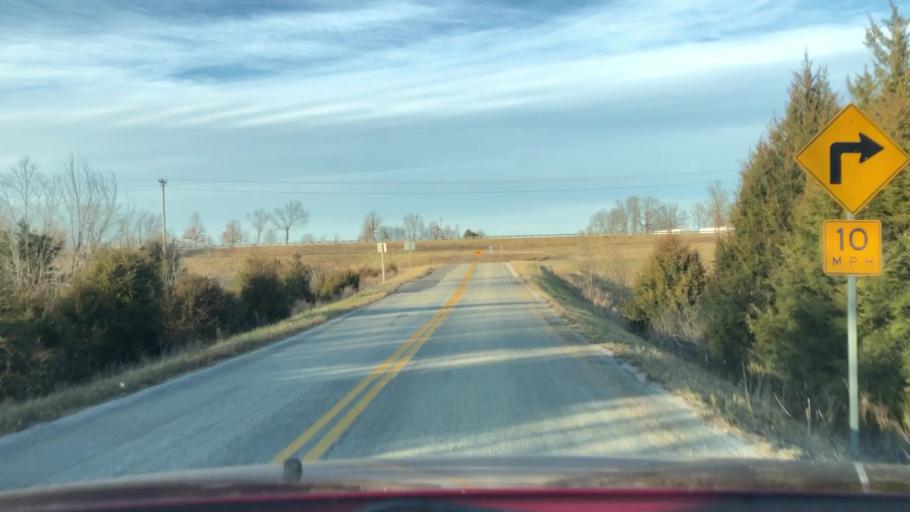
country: US
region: Missouri
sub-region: Wright County
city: Mansfield
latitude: 37.1118
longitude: -92.6295
